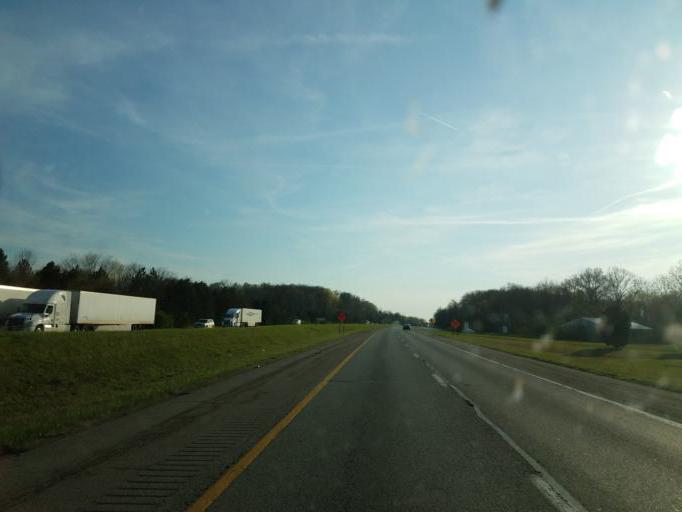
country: US
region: Ohio
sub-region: Warren County
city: Morrow
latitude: 39.4278
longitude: -84.0829
